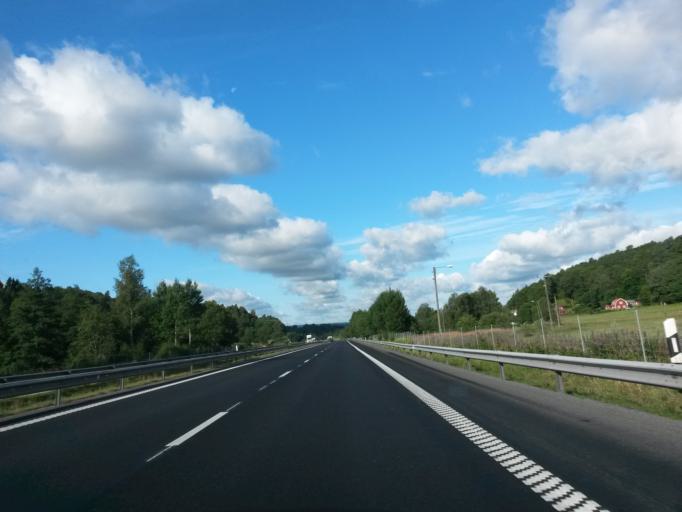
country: SE
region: Vaestra Goetaland
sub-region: Lerums Kommun
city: Stenkullen
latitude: 57.7880
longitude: 12.3284
